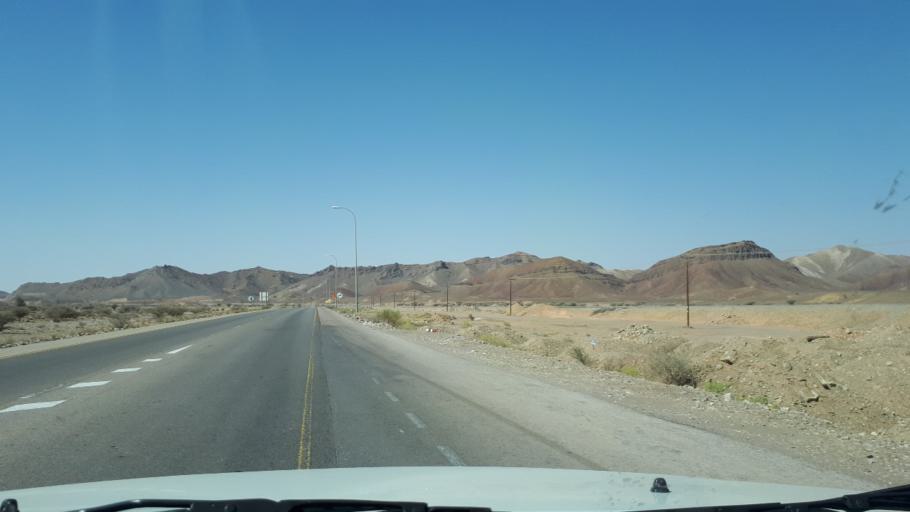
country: OM
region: Ash Sharqiyah
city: Sur
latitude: 22.3699
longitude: 59.3163
